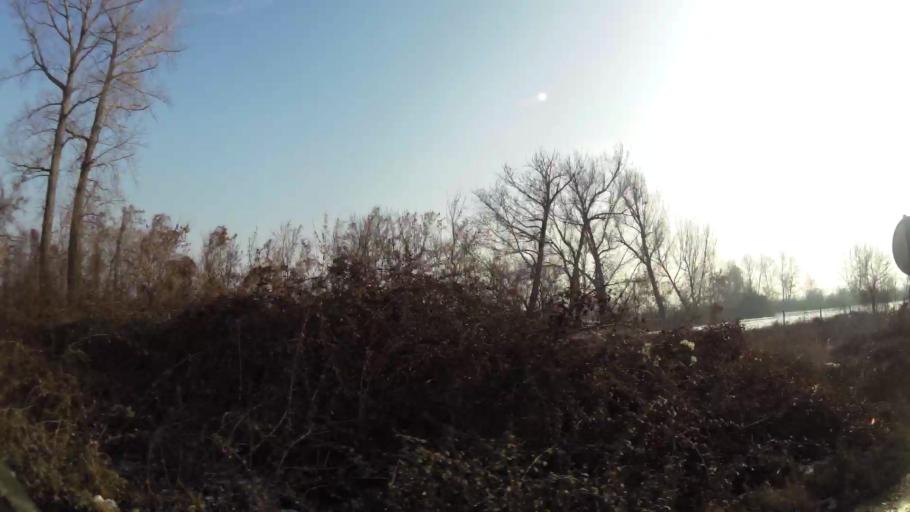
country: MK
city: Kadino
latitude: 41.9606
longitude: 21.5907
